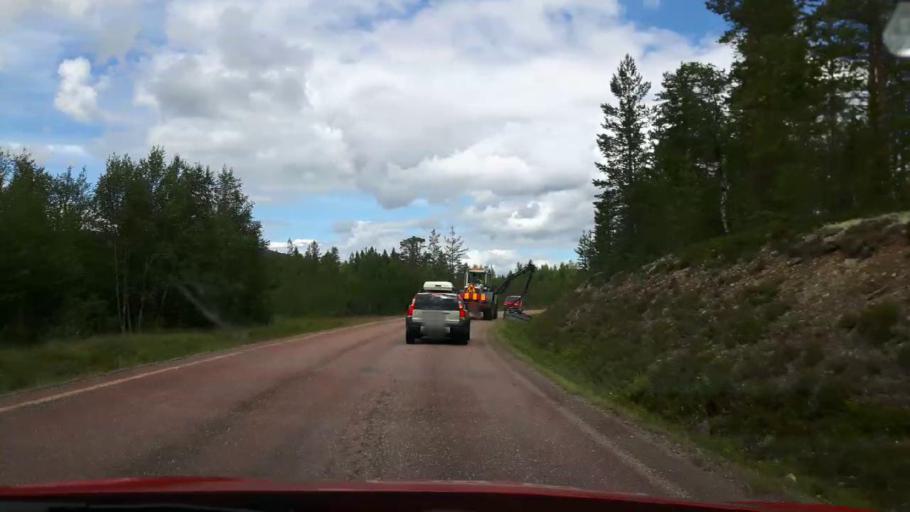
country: NO
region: Hedmark
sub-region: Trysil
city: Innbygda
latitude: 61.8964
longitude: 12.9874
